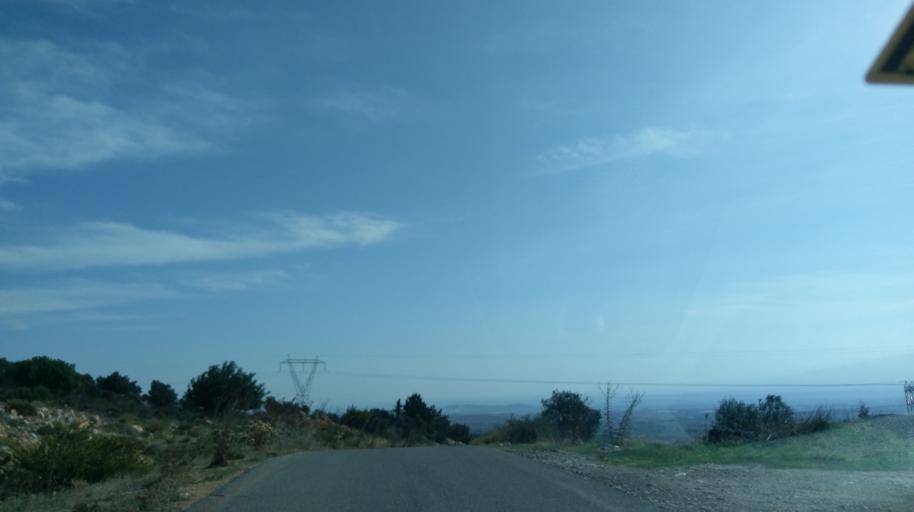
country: CY
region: Keryneia
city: Lapithos
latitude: 35.3014
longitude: 33.1580
